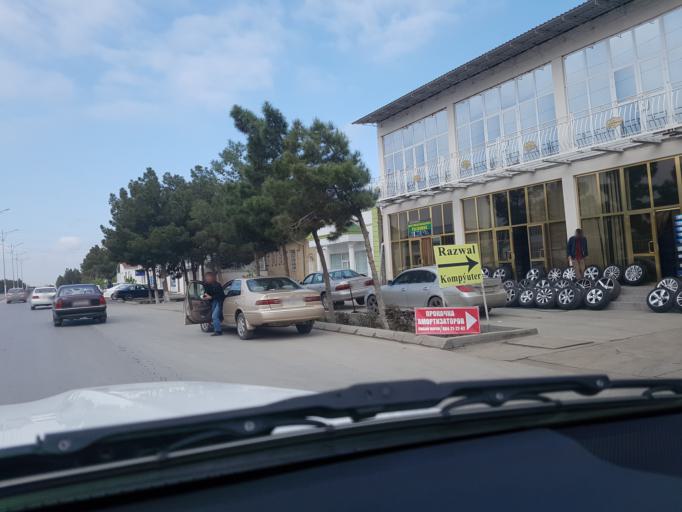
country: TM
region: Lebap
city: Turkmenabat
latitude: 39.0725
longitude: 63.5943
